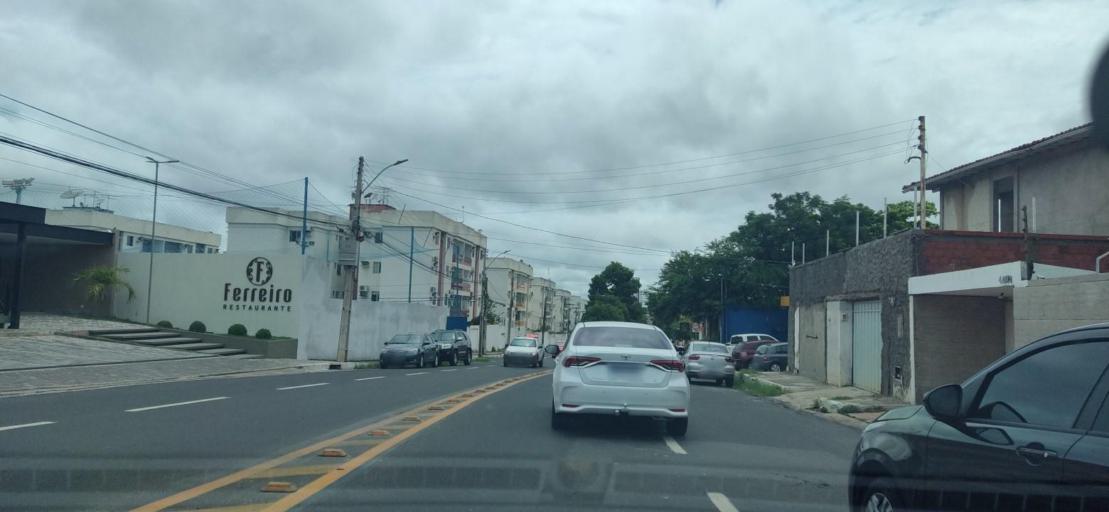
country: BR
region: Piaui
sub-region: Teresina
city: Teresina
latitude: -5.0700
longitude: -42.7601
